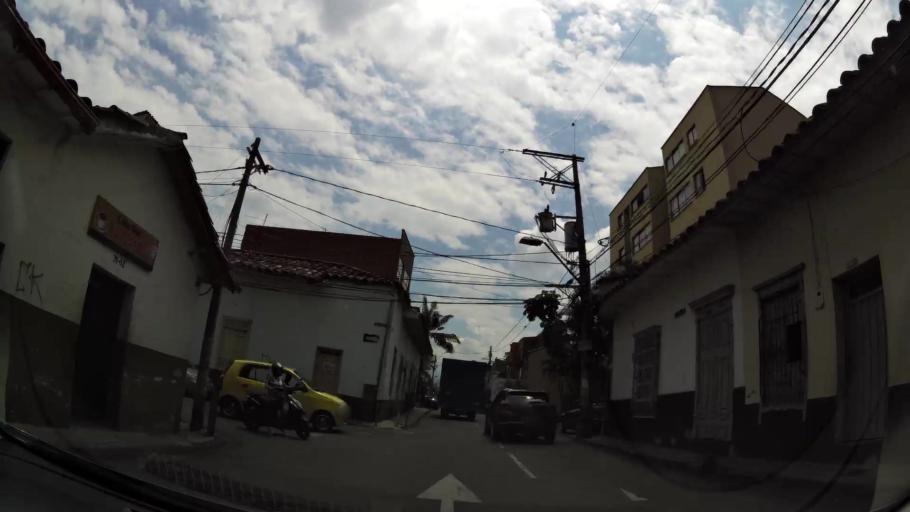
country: CO
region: Antioquia
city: Medellin
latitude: 6.2328
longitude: -75.5982
